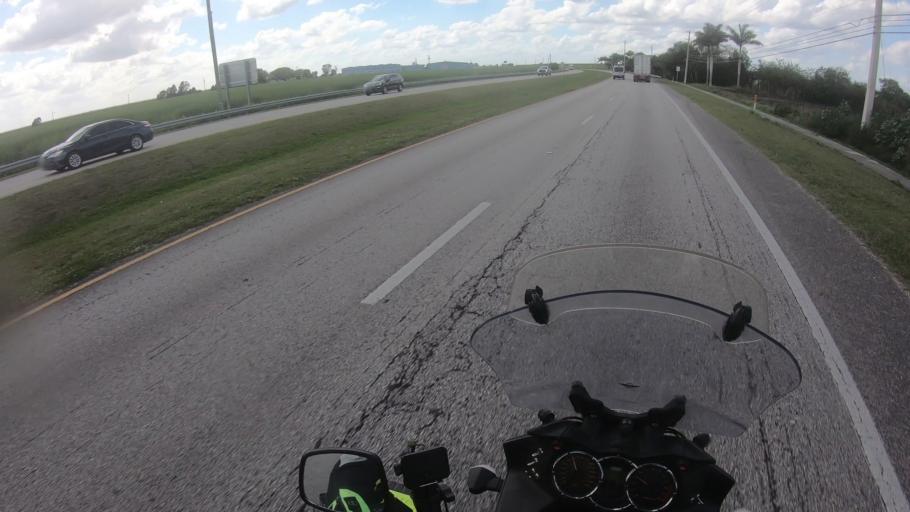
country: US
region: Florida
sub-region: Palm Beach County
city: South Bay
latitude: 26.6787
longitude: -80.7272
